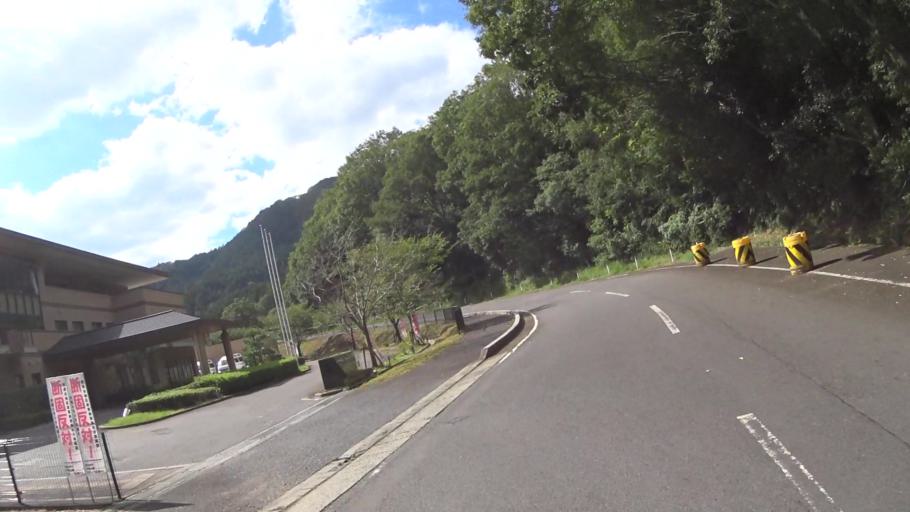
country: JP
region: Shiga Prefecture
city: Otsu-shi
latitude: 34.9496
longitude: 135.8861
